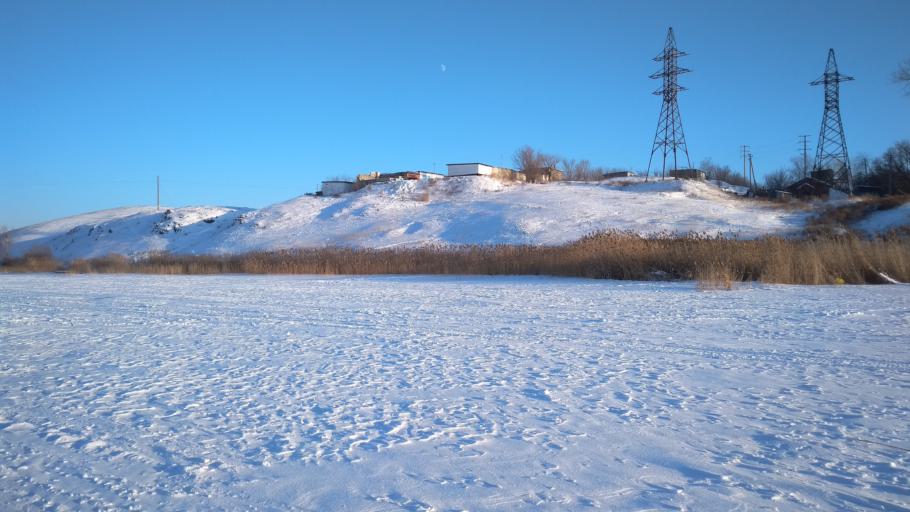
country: RU
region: Chelyabinsk
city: Troitsk
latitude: 54.0803
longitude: 61.5801
